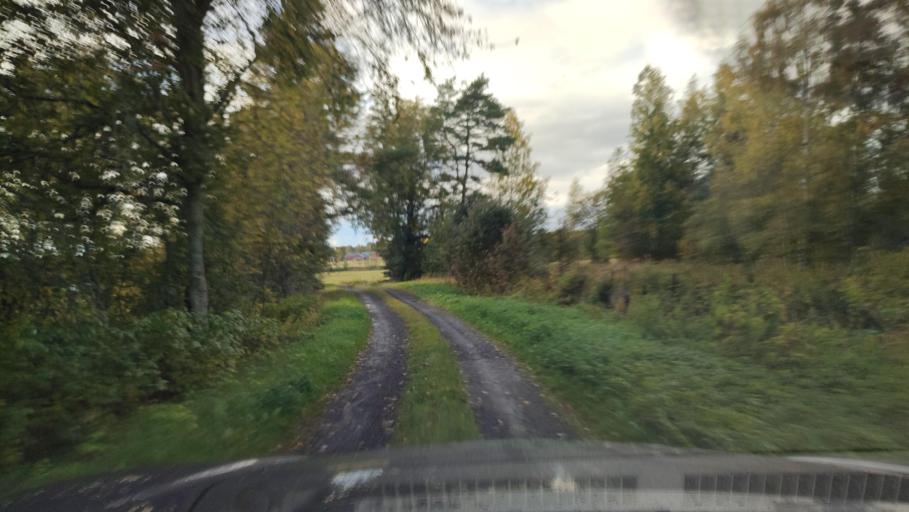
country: FI
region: Ostrobothnia
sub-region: Sydosterbotten
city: Kristinestad
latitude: 62.3060
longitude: 21.5025
